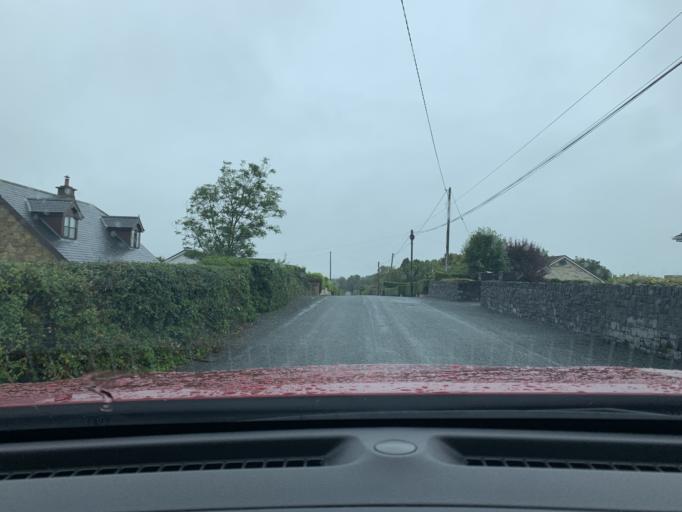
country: IE
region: Connaught
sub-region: Sligo
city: Sligo
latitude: 54.3073
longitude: -8.4646
